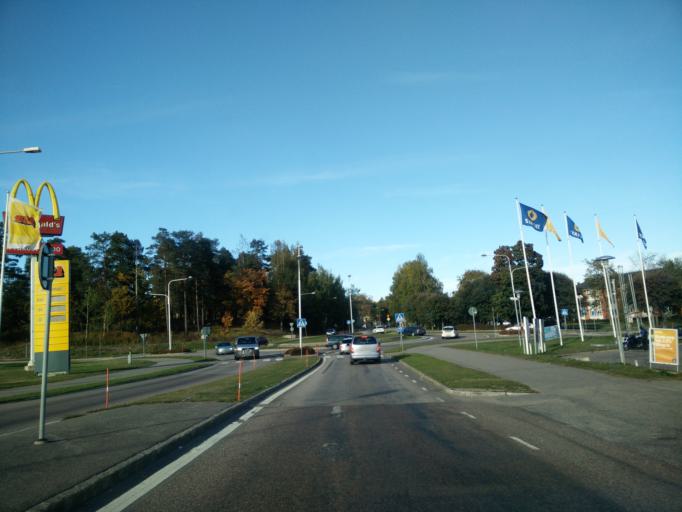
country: SE
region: Gaevleborg
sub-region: Hudiksvalls Kommun
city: Hudiksvall
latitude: 61.7336
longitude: 17.1003
